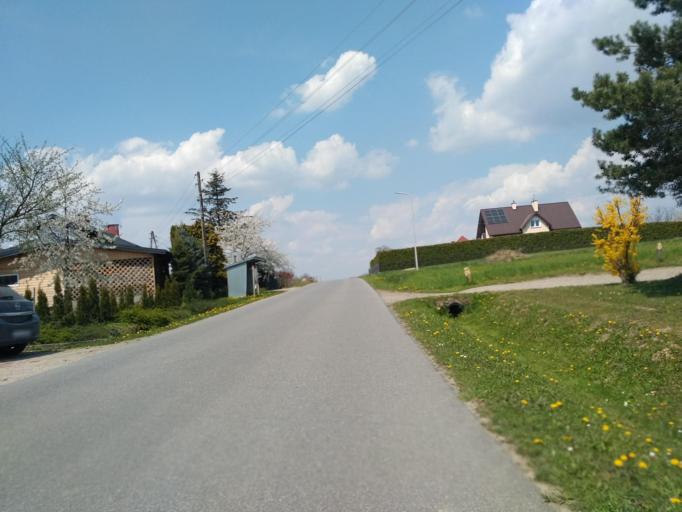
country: PL
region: Subcarpathian Voivodeship
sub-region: Powiat jasielski
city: Debowiec
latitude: 49.6937
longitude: 21.5125
